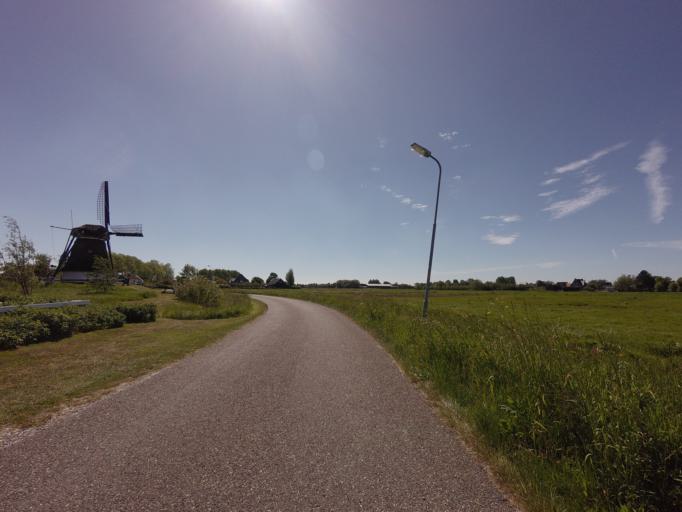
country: NL
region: North Holland
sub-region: Gemeente Uitgeest
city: Uitgeest
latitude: 52.5703
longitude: 4.7433
